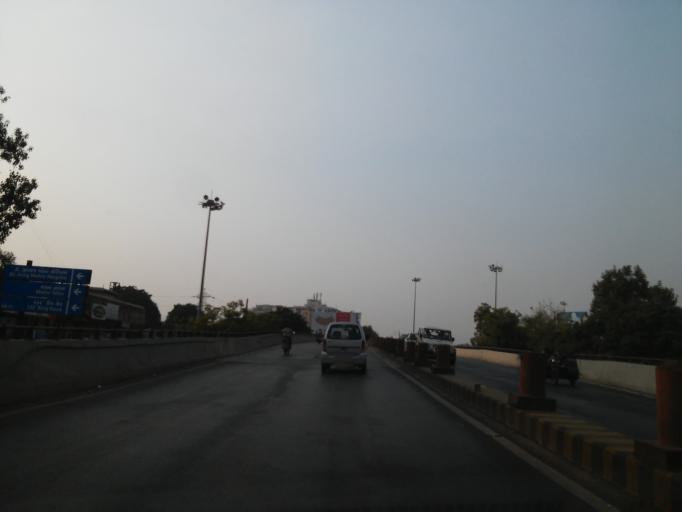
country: IN
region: Gujarat
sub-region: Ahmadabad
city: Ahmedabad
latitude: 23.0102
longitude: 72.5470
